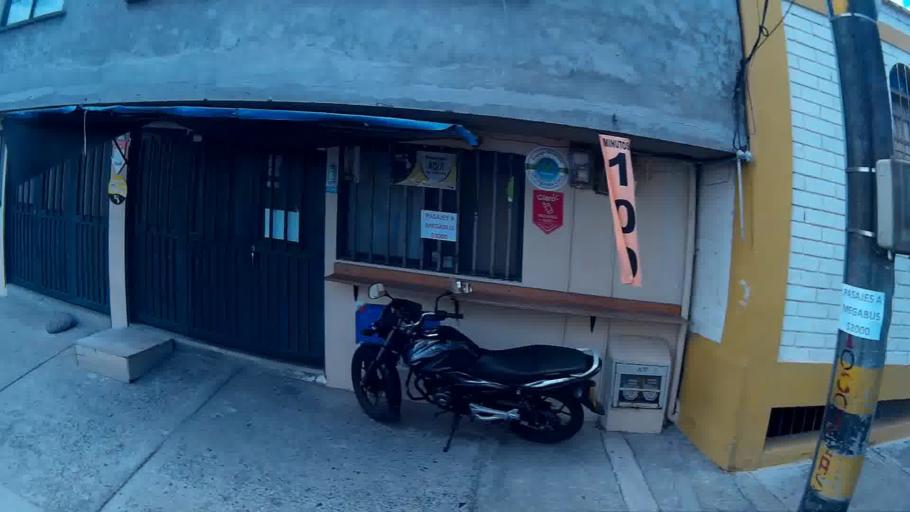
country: CO
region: Valle del Cauca
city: Ulloa
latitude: 4.7415
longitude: -75.7141
